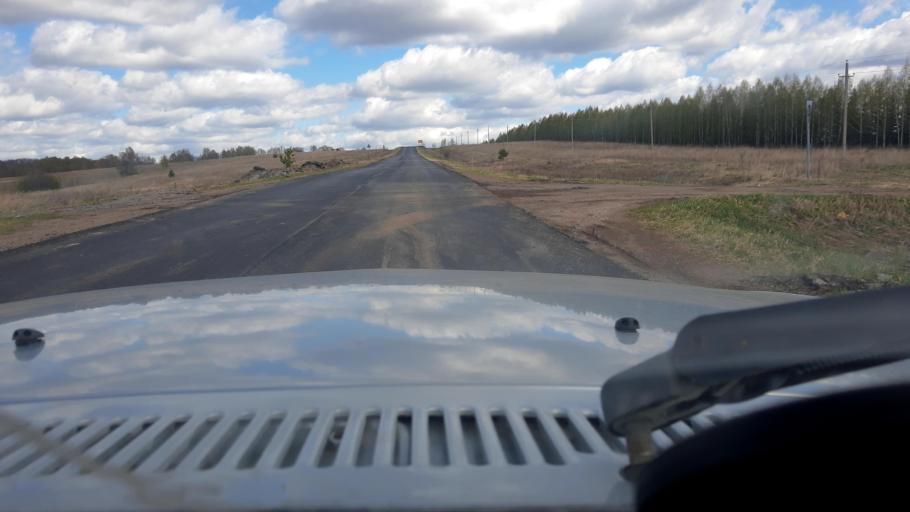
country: RU
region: Bashkortostan
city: Pavlovka
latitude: 55.3575
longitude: 56.4074
